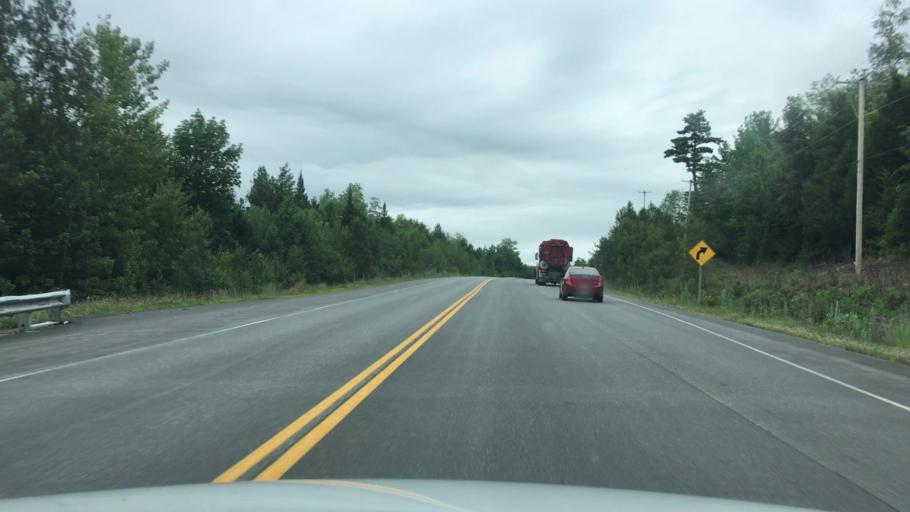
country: US
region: Maine
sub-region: Hancock County
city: Franklin
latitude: 44.8433
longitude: -68.3427
